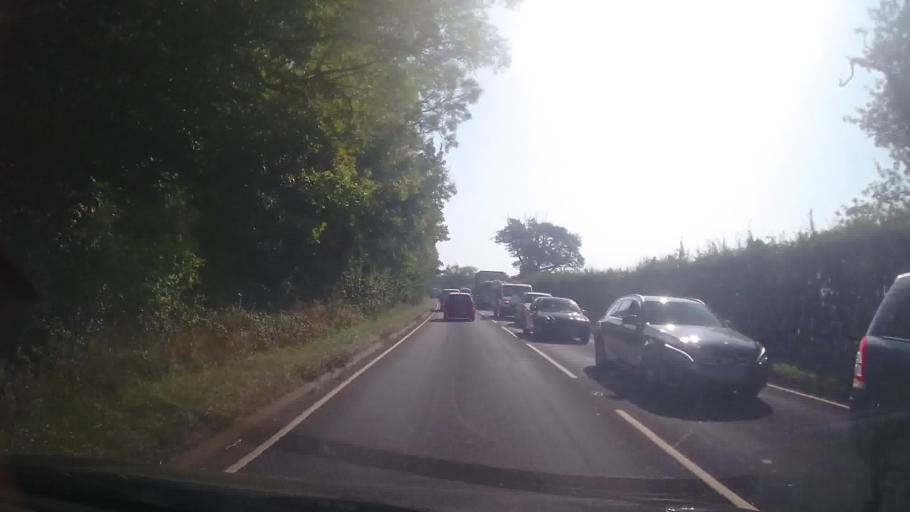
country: GB
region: England
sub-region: Worcestershire
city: Evesham
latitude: 52.1225
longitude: -1.9801
